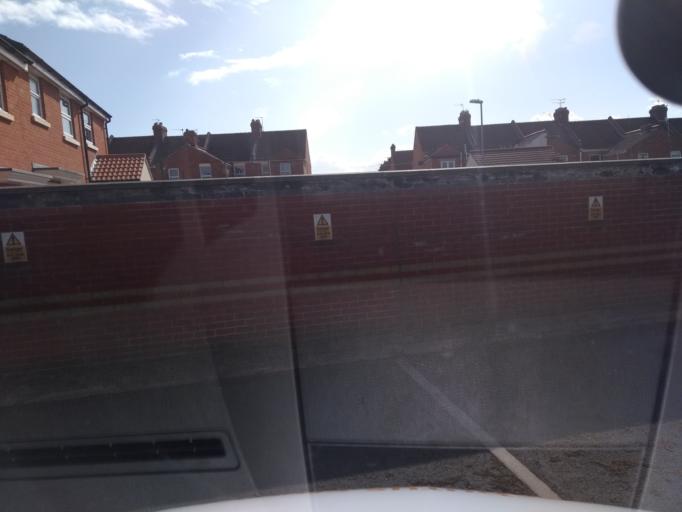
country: GB
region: England
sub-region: Somerset
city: Bridgwater
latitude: 51.1298
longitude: -3.0148
